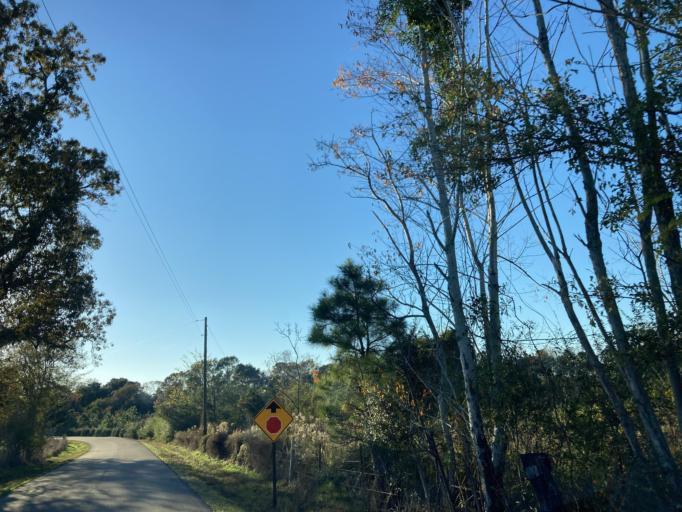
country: US
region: Mississippi
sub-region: Lamar County
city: Sumrall
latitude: 31.2677
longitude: -89.6009
